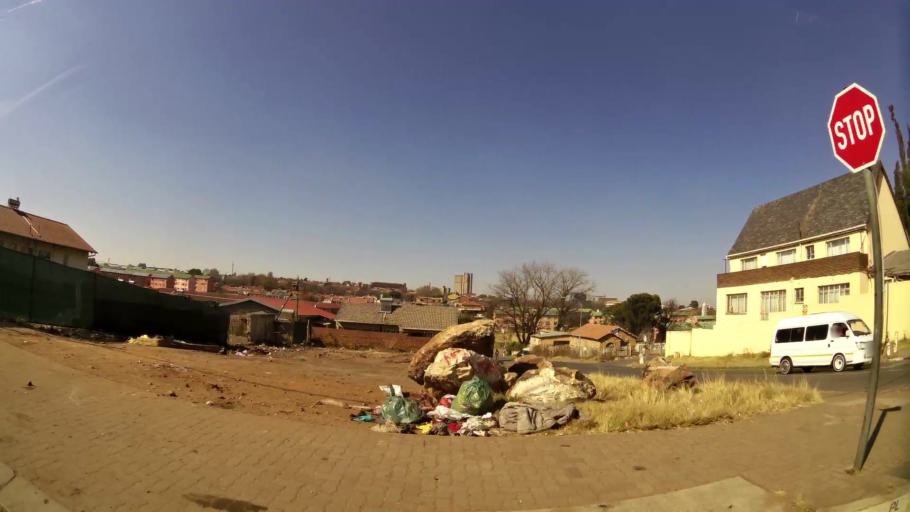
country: ZA
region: Gauteng
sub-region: City of Johannesburg Metropolitan Municipality
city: Johannesburg
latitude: -26.1837
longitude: 27.9647
